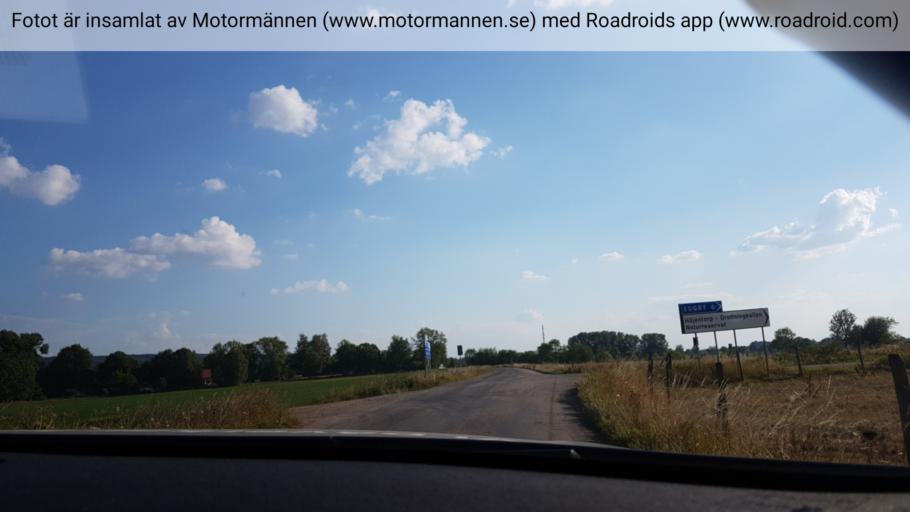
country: SE
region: Vaestra Goetaland
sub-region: Skara Kommun
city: Axvall
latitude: 58.3935
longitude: 13.6547
